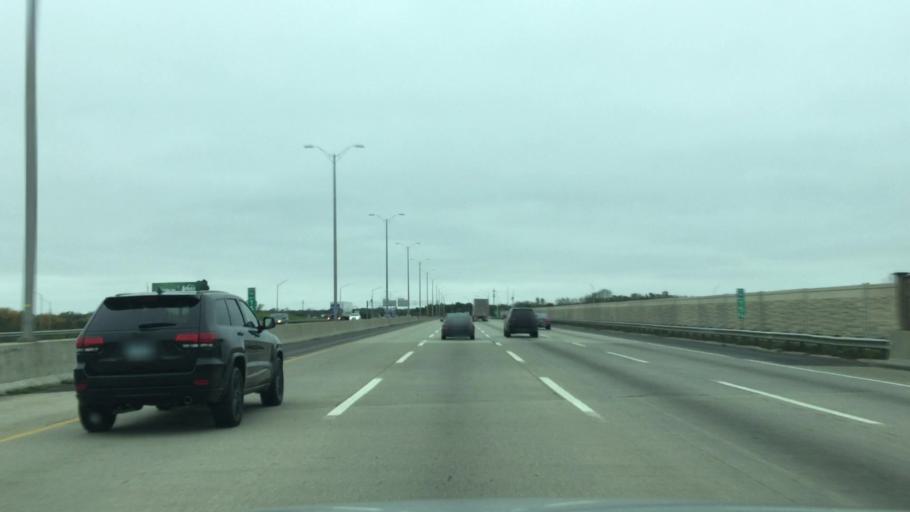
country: US
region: Illinois
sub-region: Lake County
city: Green Oaks
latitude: 42.2845
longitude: -87.9091
